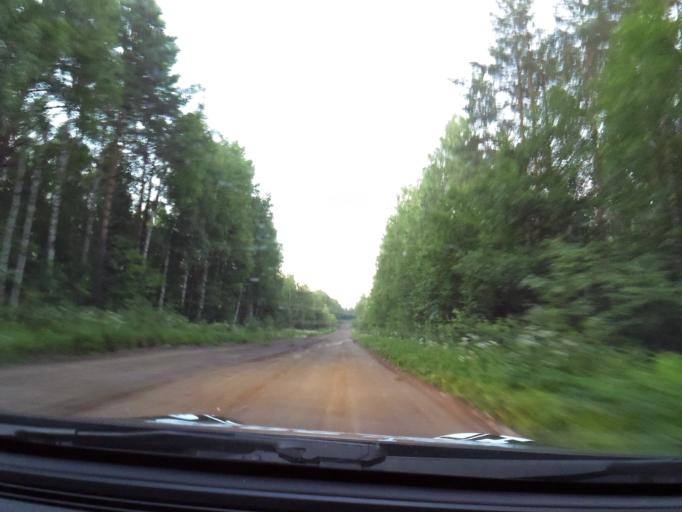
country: RU
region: Leningrad
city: Voznesen'ye
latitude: 60.8539
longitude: 35.8962
